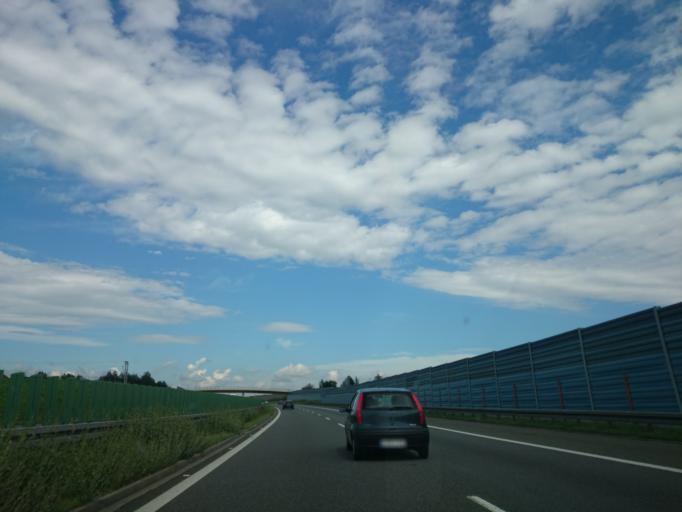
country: PL
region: Opole Voivodeship
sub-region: Powiat krapkowicki
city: Krapkowice
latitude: 50.5103
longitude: 17.9646
